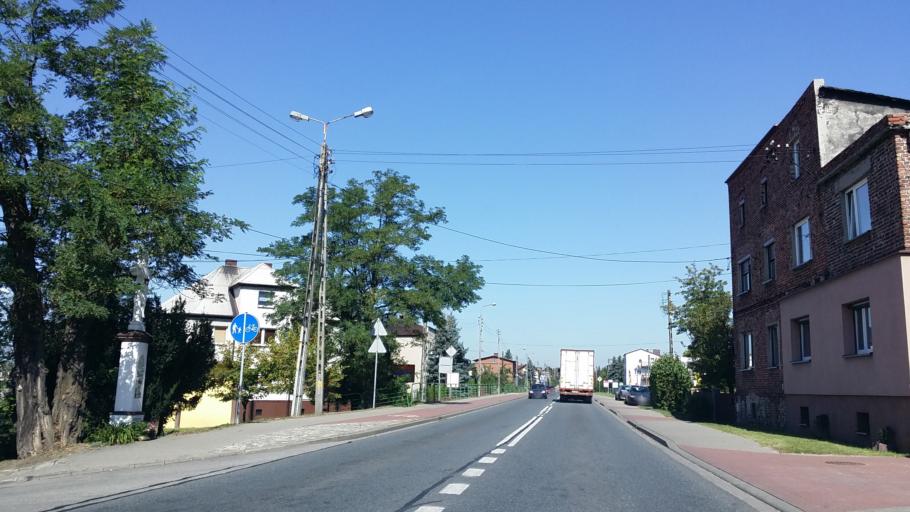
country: PL
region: Silesian Voivodeship
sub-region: Powiat bierunsko-ledzinski
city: Imielin
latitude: 50.1485
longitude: 19.1838
